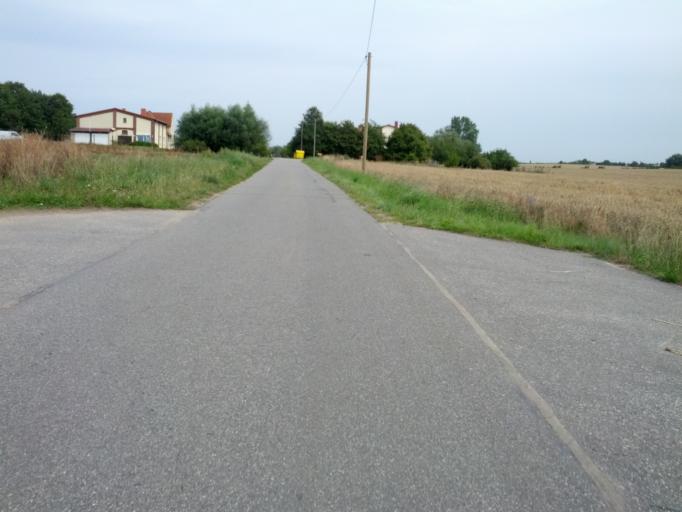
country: DE
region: Mecklenburg-Vorpommern
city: Bastorf
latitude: 54.1487
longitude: 11.6981
